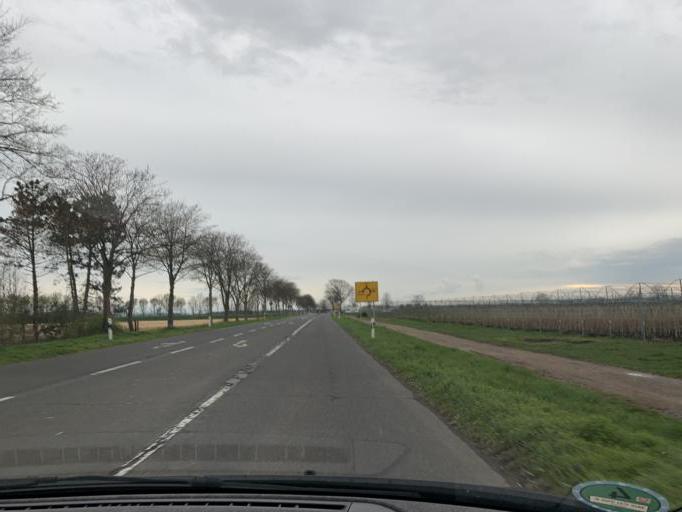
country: DE
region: North Rhine-Westphalia
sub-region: Regierungsbezirk Koln
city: Norvenich
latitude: 50.8027
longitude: 6.6918
